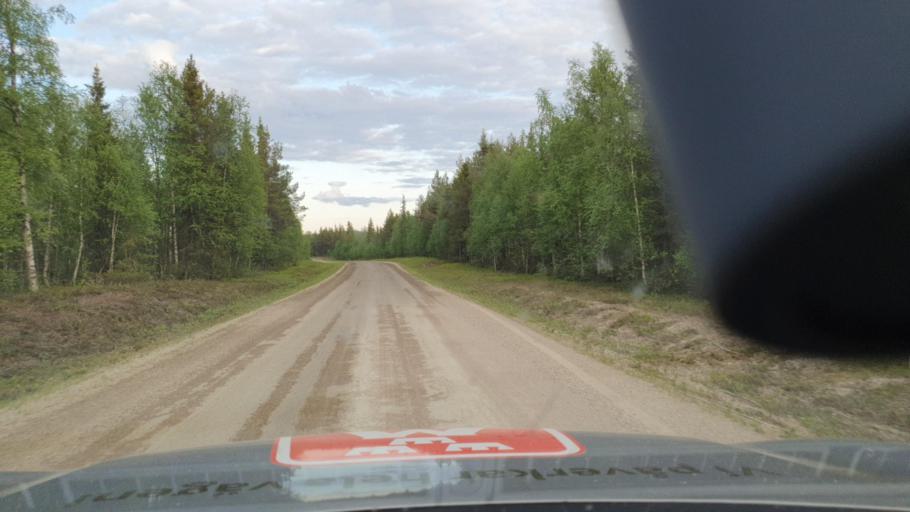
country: SE
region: Norrbotten
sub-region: Gallivare Kommun
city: Gaellivare
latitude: 66.6869
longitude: 21.1812
